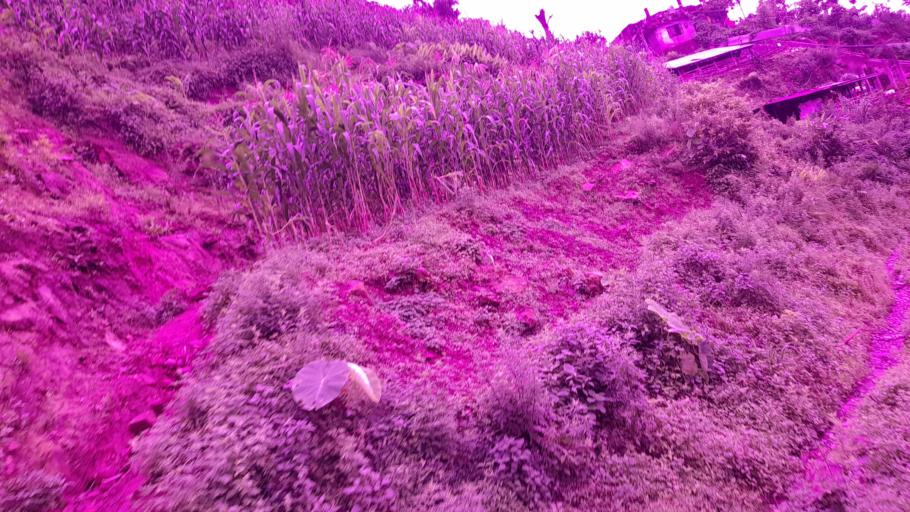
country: NP
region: Central Region
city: Kirtipur
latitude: 27.8163
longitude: 85.2137
